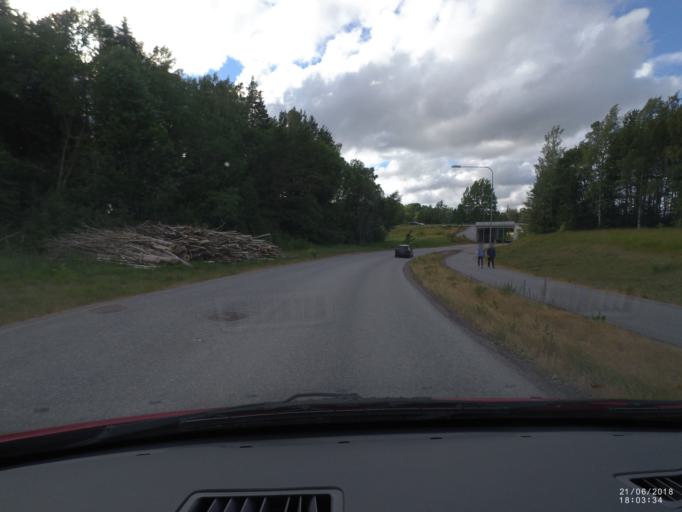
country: SE
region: Soedermanland
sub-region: Nykopings Kommun
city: Nykoping
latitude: 58.7688
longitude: 17.0078
